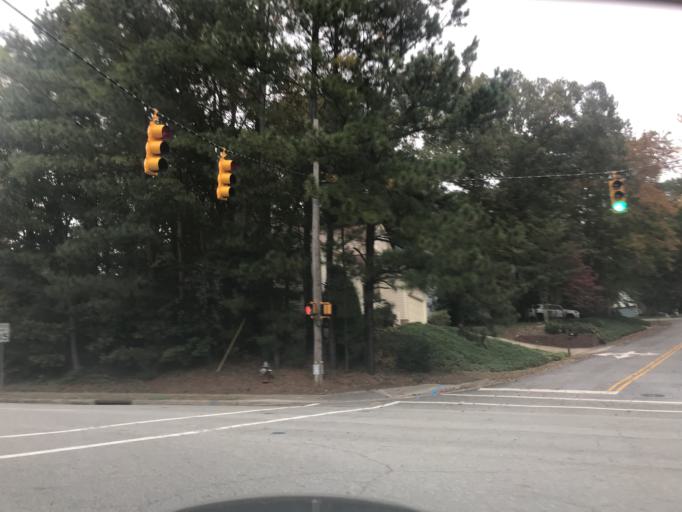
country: US
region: North Carolina
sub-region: Wake County
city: West Raleigh
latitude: 35.8942
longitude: -78.6637
